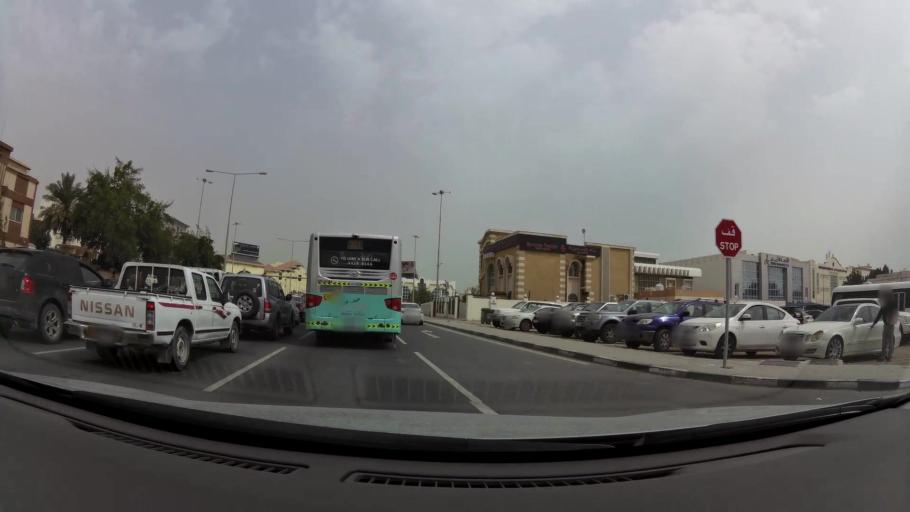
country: QA
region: Baladiyat ad Dawhah
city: Doha
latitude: 25.2619
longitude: 51.5379
